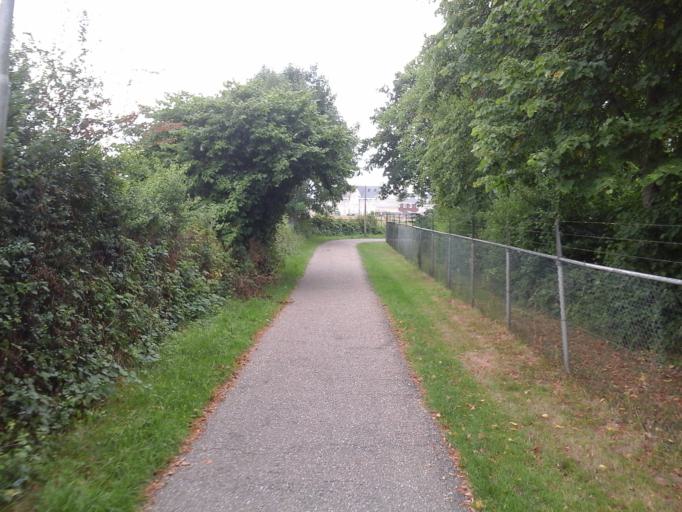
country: NL
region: Gelderland
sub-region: Gemeente Geldermalsen
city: Geldermalsen
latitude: 51.8862
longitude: 5.2759
